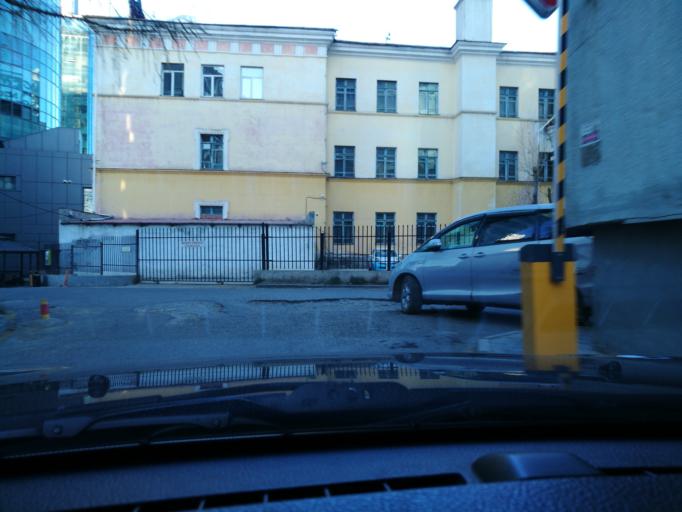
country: MN
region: Ulaanbaatar
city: Ulaanbaatar
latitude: 47.9145
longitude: 106.9169
